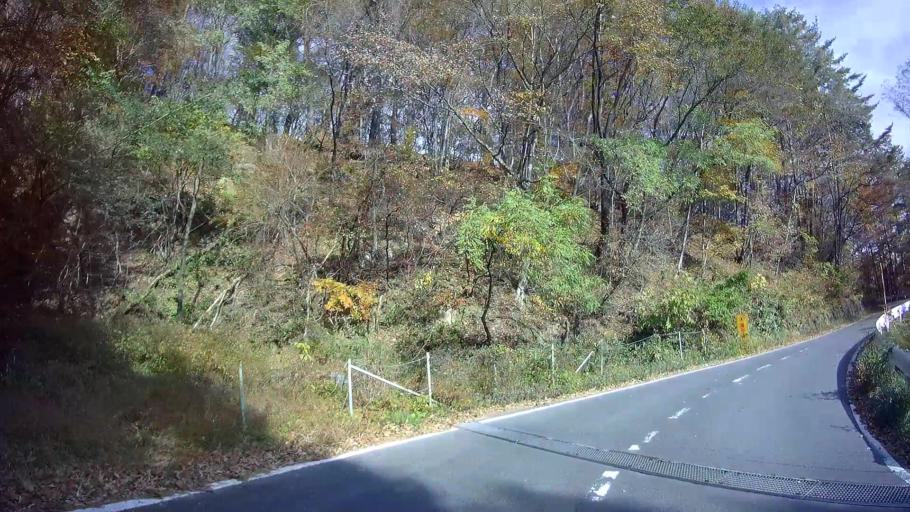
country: JP
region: Gunma
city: Nakanojomachi
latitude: 36.6191
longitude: 138.6348
